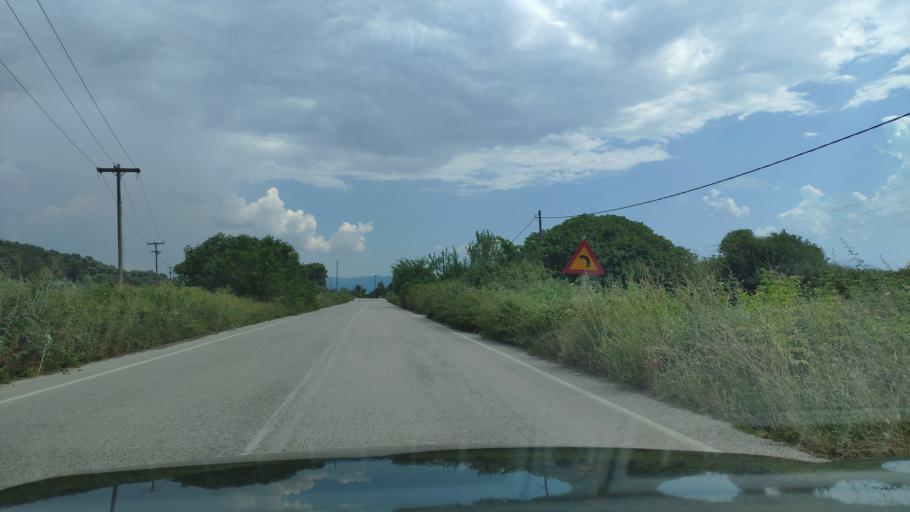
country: GR
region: West Greece
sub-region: Nomos Aitolias kai Akarnanias
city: Krikellos
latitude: 38.9683
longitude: 21.1682
